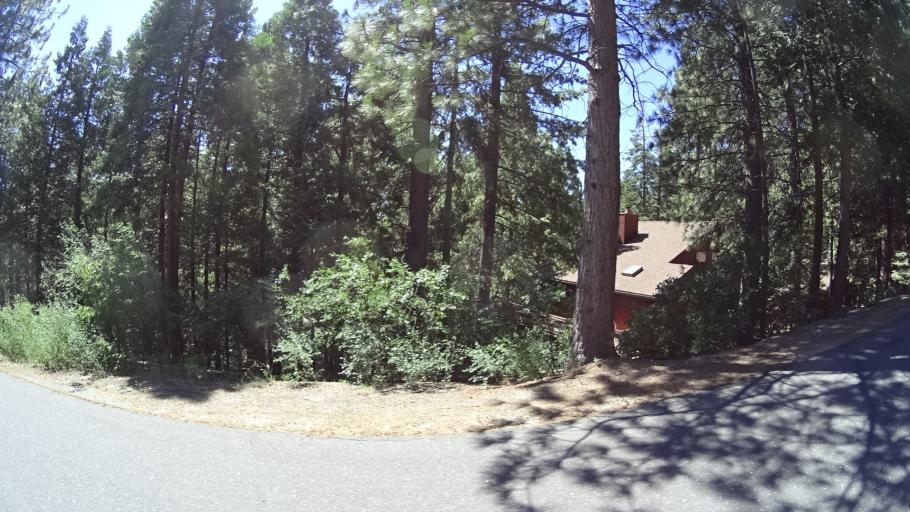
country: US
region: California
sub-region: Calaveras County
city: Arnold
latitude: 38.2919
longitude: -120.2859
